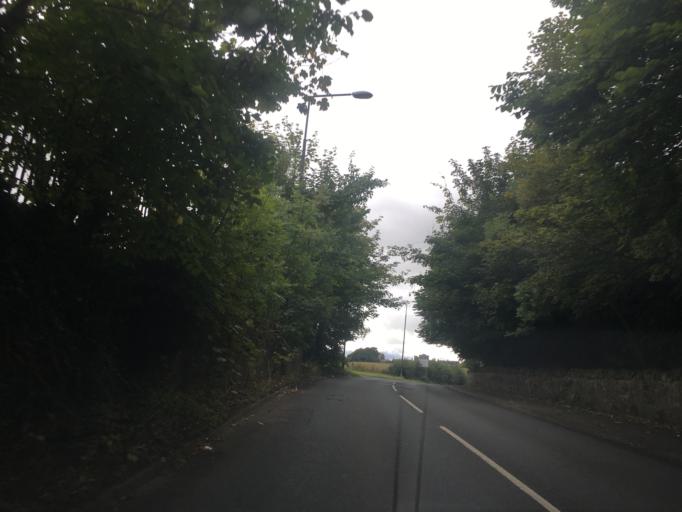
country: GB
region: Scotland
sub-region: Midlothian
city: Dalkeith
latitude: 55.8766
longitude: -3.0680
